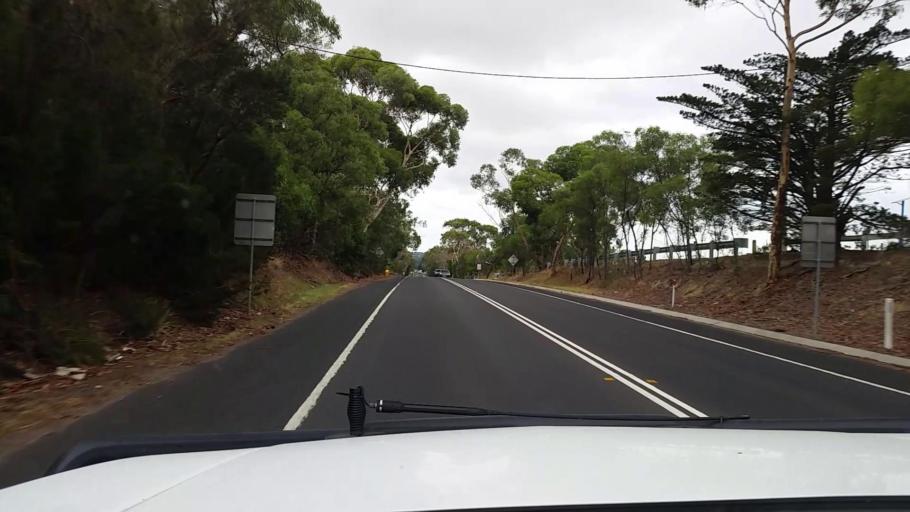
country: AU
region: Victoria
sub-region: Mornington Peninsula
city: Somerville
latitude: -38.2183
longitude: 145.1718
